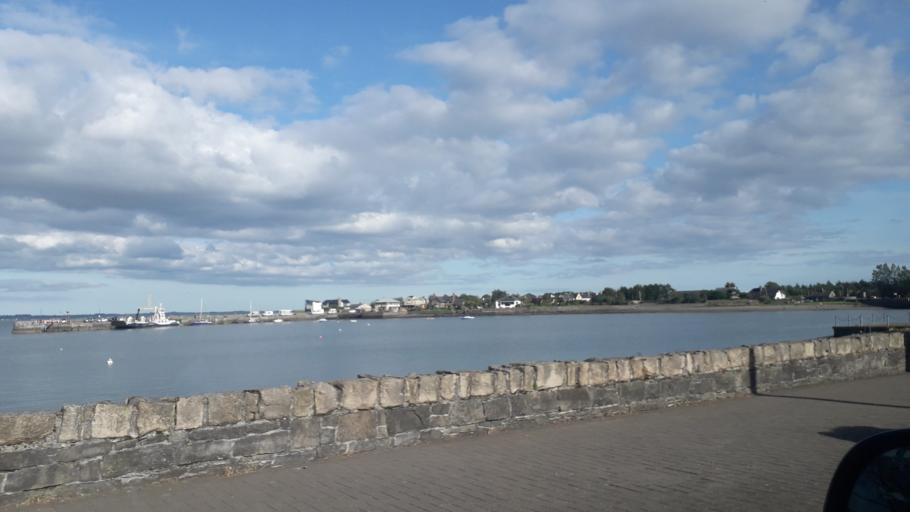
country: IE
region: Leinster
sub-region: Lu
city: Carlingford
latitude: 54.0422
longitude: -6.1866
